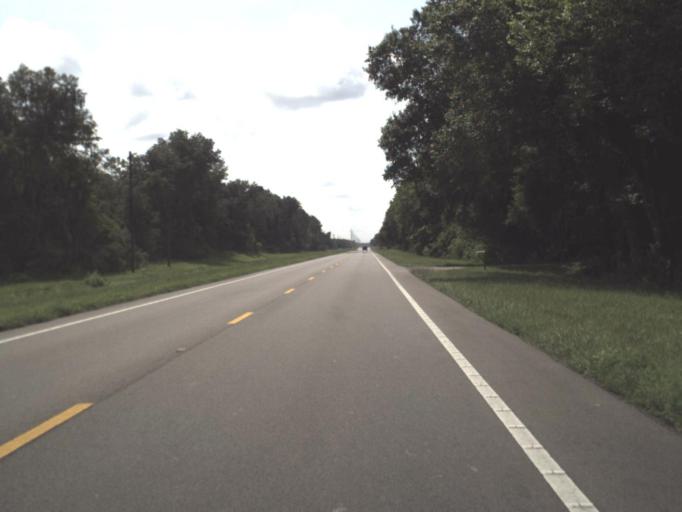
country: US
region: Florida
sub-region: Pasco County
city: Zephyrhills North
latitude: 28.2676
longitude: -82.0907
